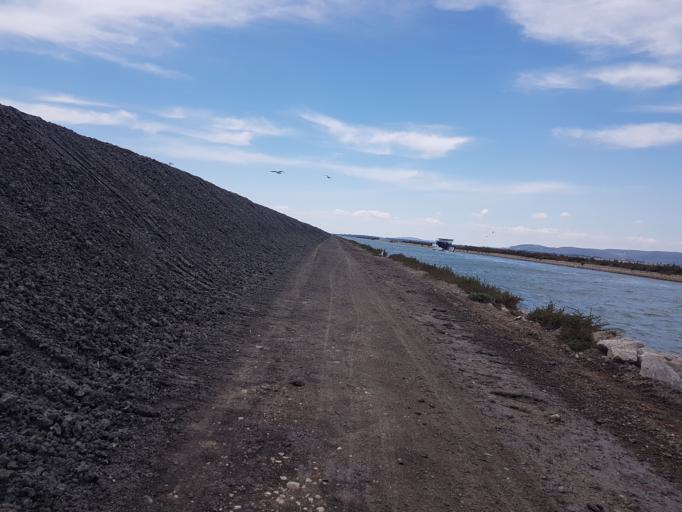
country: FR
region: Languedoc-Roussillon
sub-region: Departement de l'Herault
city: Villeneuve-les-Maguelone
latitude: 43.5036
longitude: 3.8631
